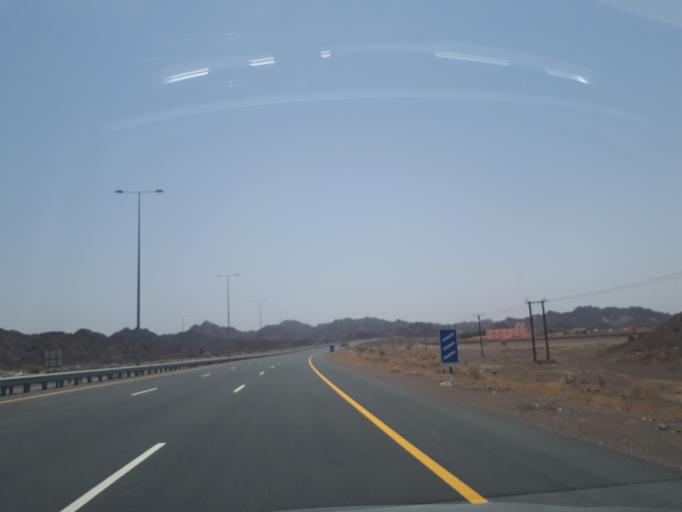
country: OM
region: Ash Sharqiyah
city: Ibra'
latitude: 22.7282
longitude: 58.5688
